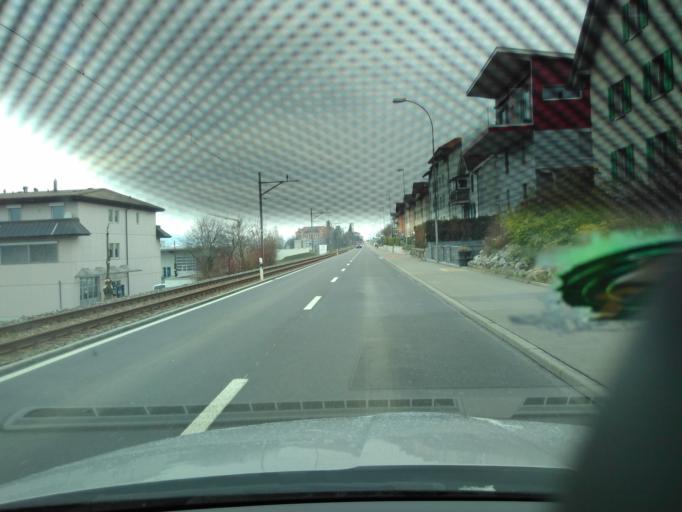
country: CH
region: Lucerne
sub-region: Hochdorf District
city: Hochdorf
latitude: 47.1749
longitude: 8.2844
